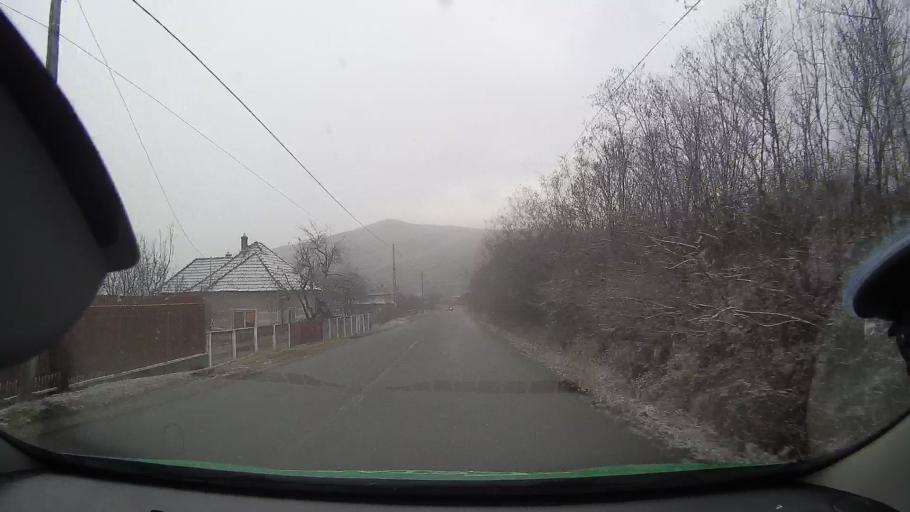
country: RO
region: Alba
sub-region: Comuna Noslac
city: Noslac
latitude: 46.3640
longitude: 23.9317
